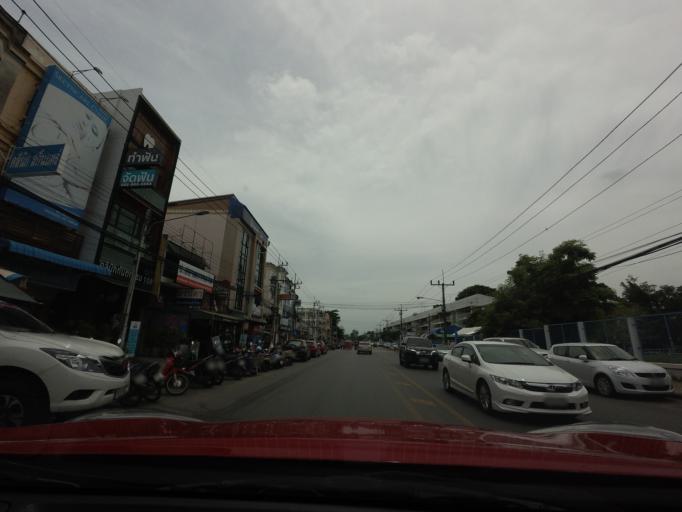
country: TH
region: Songkhla
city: Hat Yai
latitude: 7.0018
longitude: 100.4978
